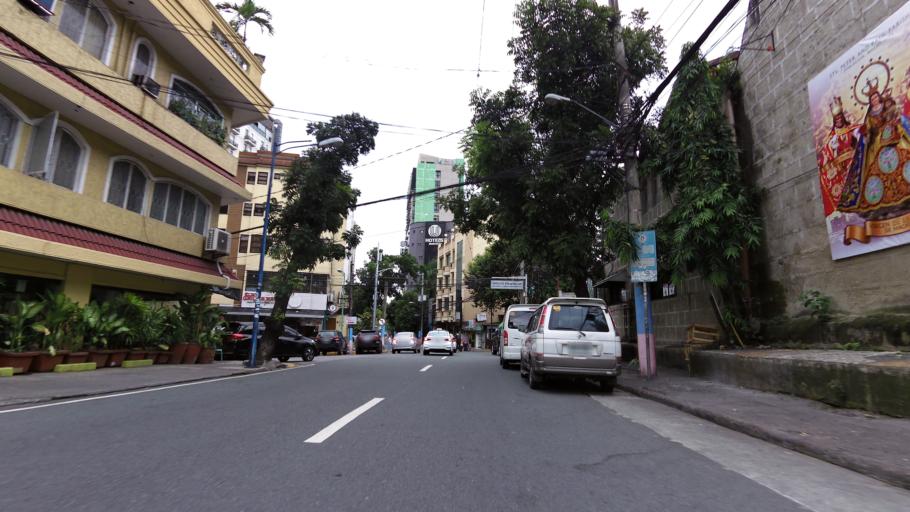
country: PH
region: Metro Manila
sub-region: Makati City
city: Makati City
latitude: 14.5658
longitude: 121.0311
